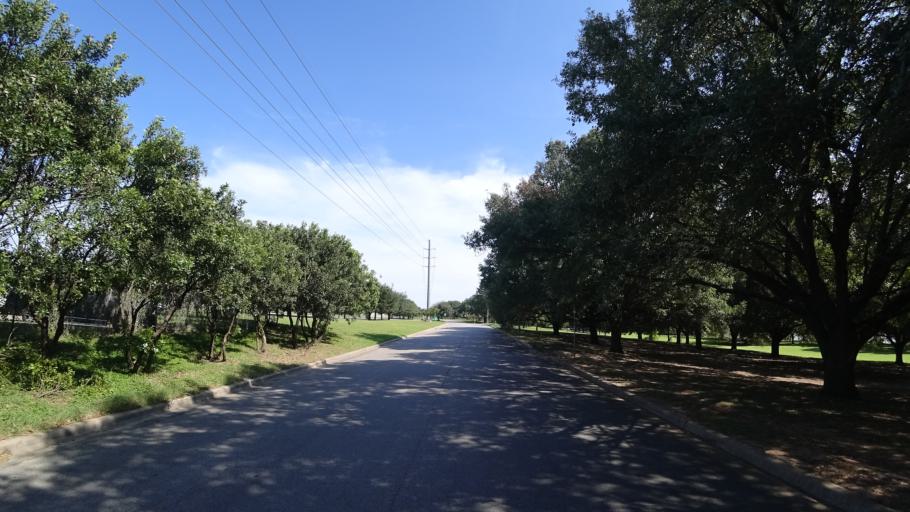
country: US
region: Texas
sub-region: Travis County
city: Austin
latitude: 30.2516
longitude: -97.7335
